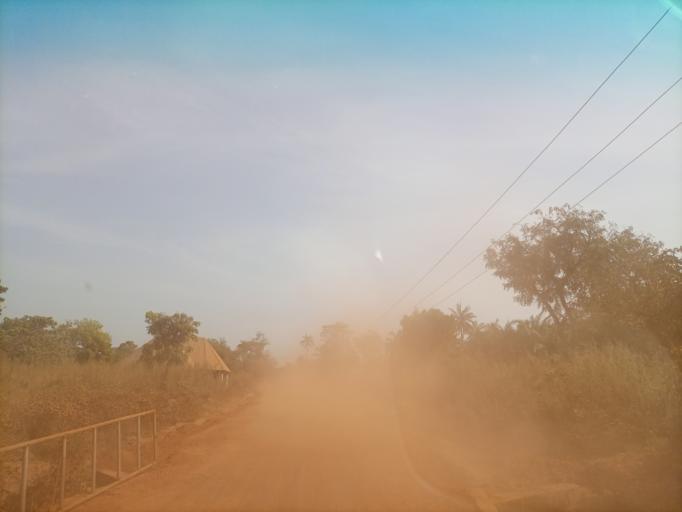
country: NG
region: Enugu
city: Eha Amufu
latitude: 6.6671
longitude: 7.7531
